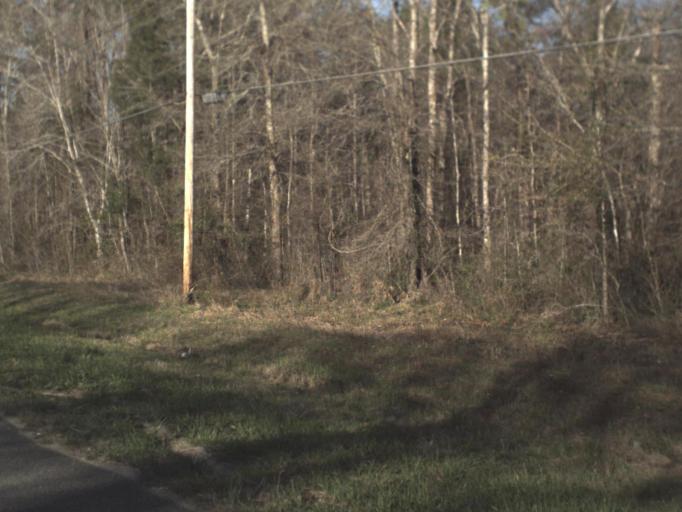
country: US
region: Florida
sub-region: Jackson County
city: Marianna
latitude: 30.7281
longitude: -85.2303
